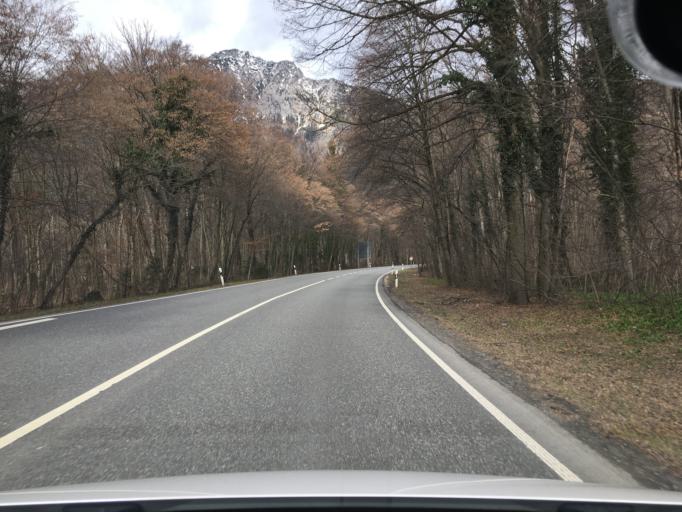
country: DE
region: Bavaria
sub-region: Upper Bavaria
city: Bad Reichenhall
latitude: 47.7249
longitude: 12.8664
